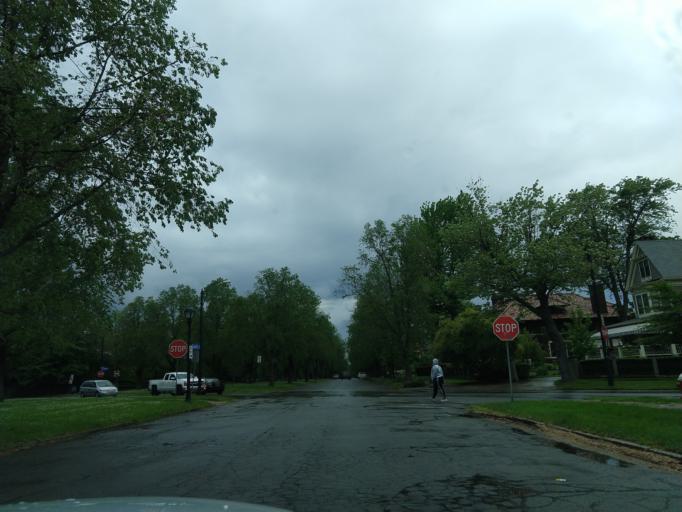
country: US
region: New York
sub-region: Erie County
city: Buffalo
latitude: 42.9220
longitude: -78.8692
